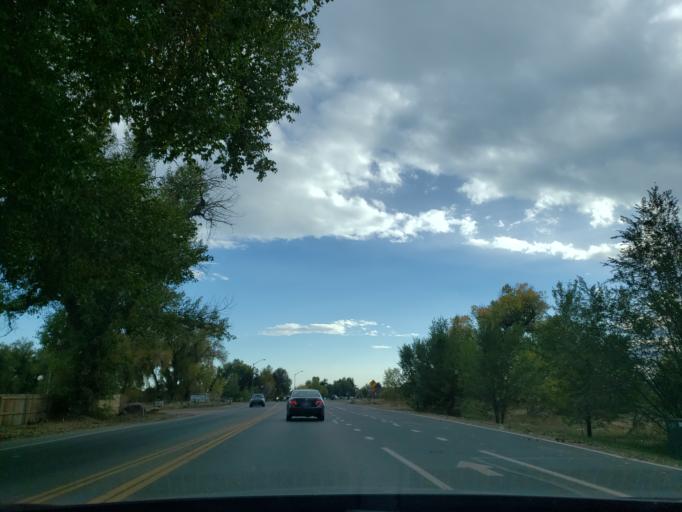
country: US
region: Colorado
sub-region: Larimer County
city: Fort Collins
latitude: 40.5891
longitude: -105.0296
